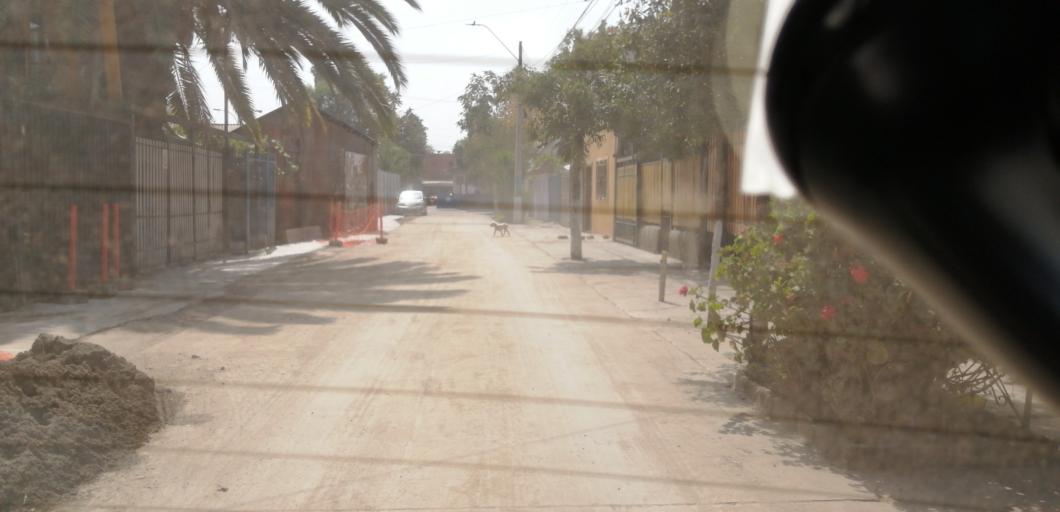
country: CL
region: Santiago Metropolitan
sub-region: Provincia de Santiago
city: Lo Prado
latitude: -33.4387
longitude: -70.7521
